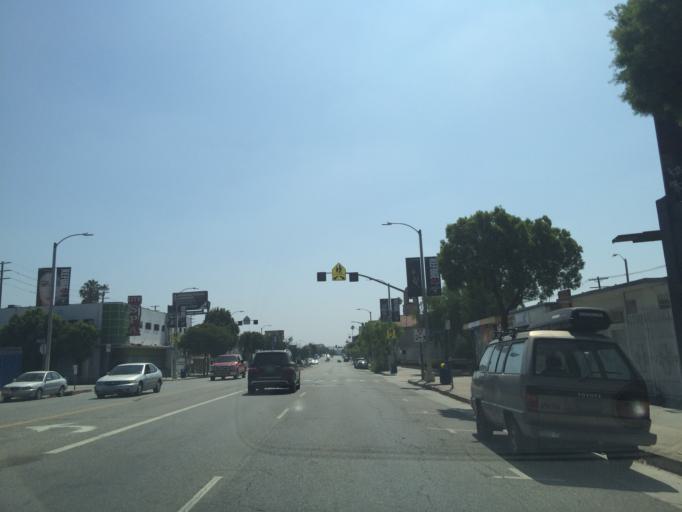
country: US
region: California
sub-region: Los Angeles County
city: West Hollywood
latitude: 34.0484
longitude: -118.3556
